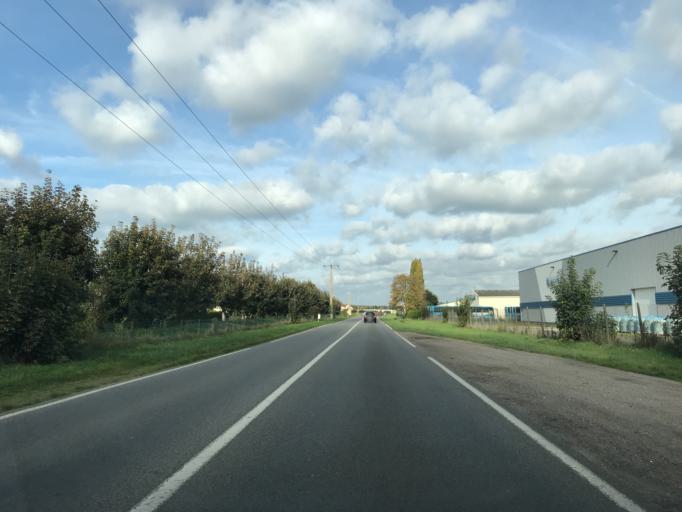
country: FR
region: Haute-Normandie
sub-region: Departement de l'Eure
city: Gaillon
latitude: 49.1646
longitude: 1.3486
